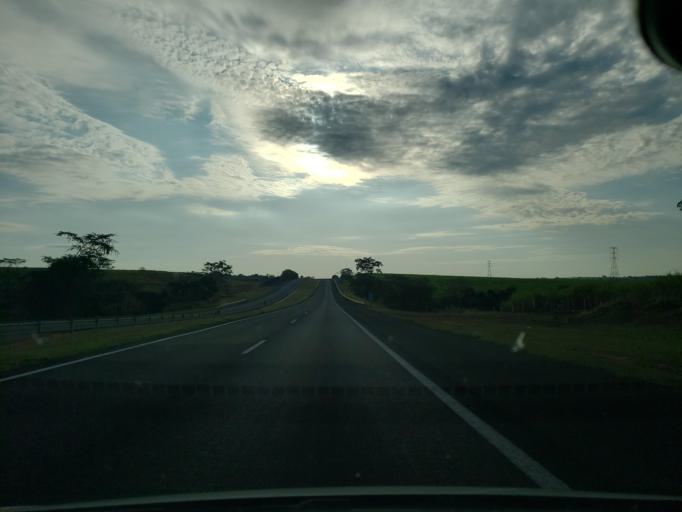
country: BR
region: Sao Paulo
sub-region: Mirandopolis
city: Mirandopolis
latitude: -21.0929
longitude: -51.0521
